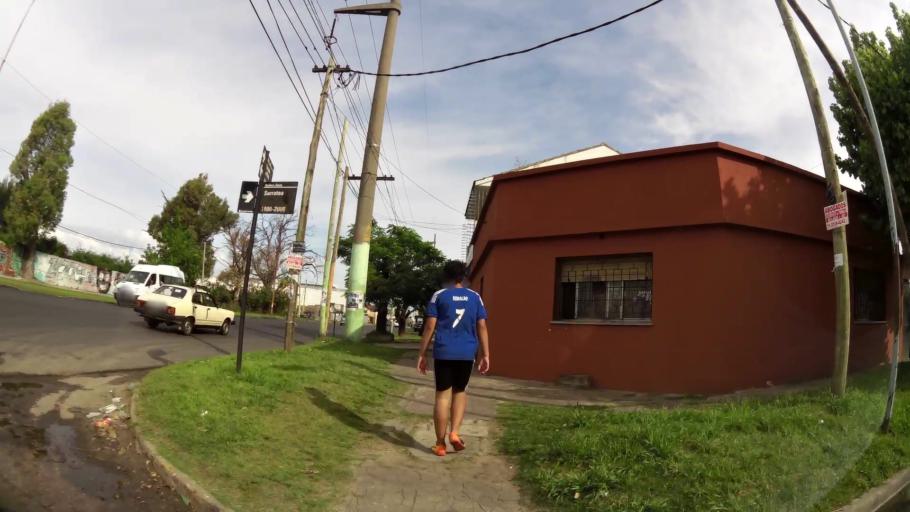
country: AR
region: Buenos Aires
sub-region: Partido de Quilmes
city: Quilmes
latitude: -34.7444
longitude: -58.2724
